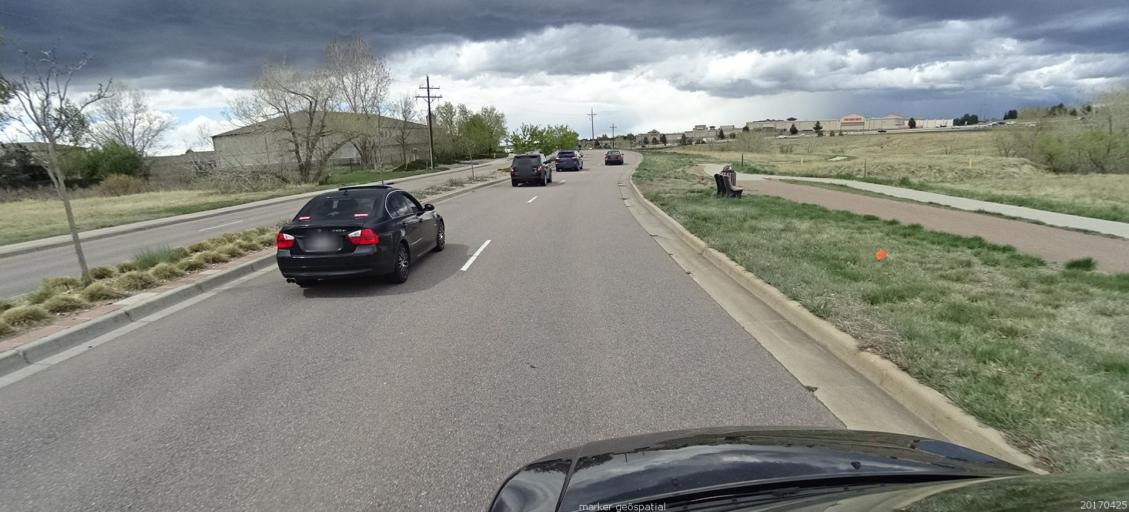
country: US
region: Colorado
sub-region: Adams County
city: Lone Tree
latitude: 39.5575
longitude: -104.8854
